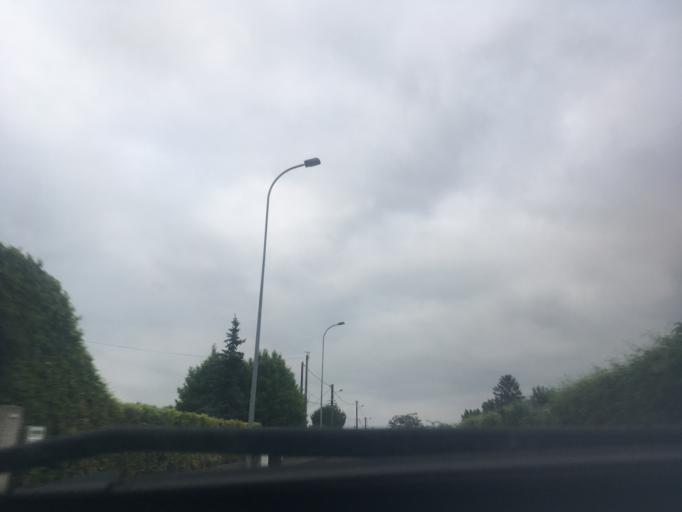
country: FR
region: Poitou-Charentes
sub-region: Departement de la Charente
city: Chateaubernard
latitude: 45.6810
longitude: -0.3333
